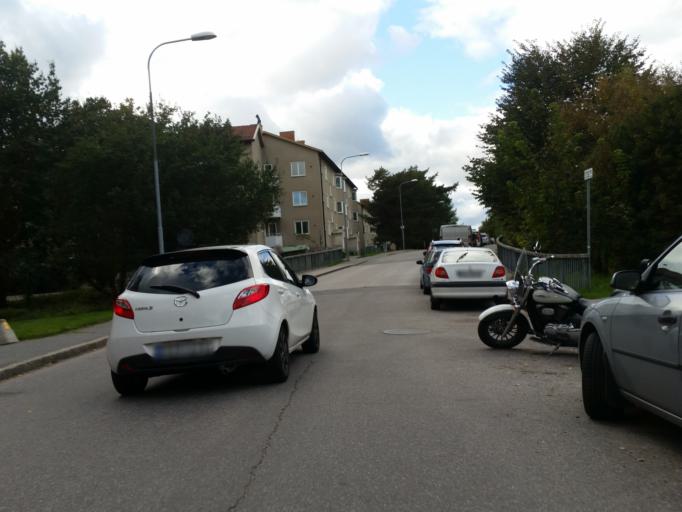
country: SE
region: Stockholm
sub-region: Stockholms Kommun
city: OEstermalm
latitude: 59.2876
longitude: 18.1064
